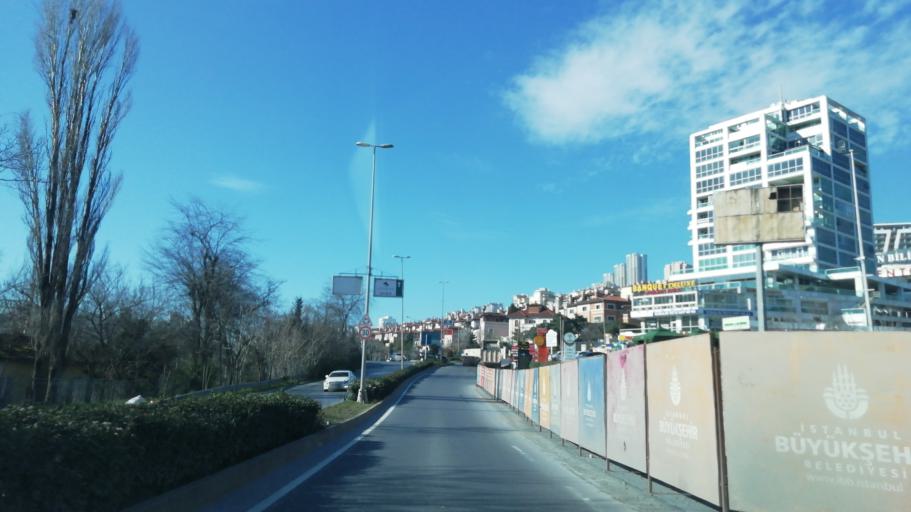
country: TR
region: Istanbul
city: Esenyurt
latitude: 41.0634
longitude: 28.6998
